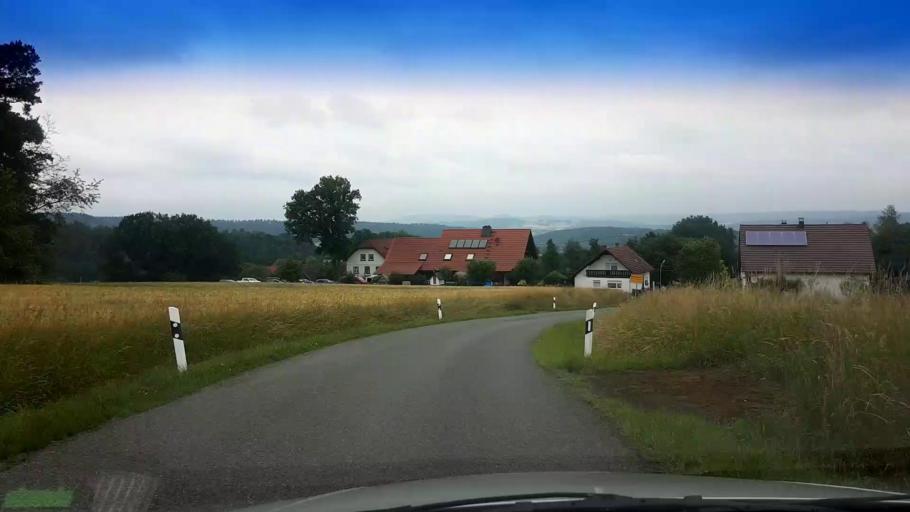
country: DE
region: Bavaria
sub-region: Upper Franconia
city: Kasendorf
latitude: 50.0780
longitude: 11.3384
